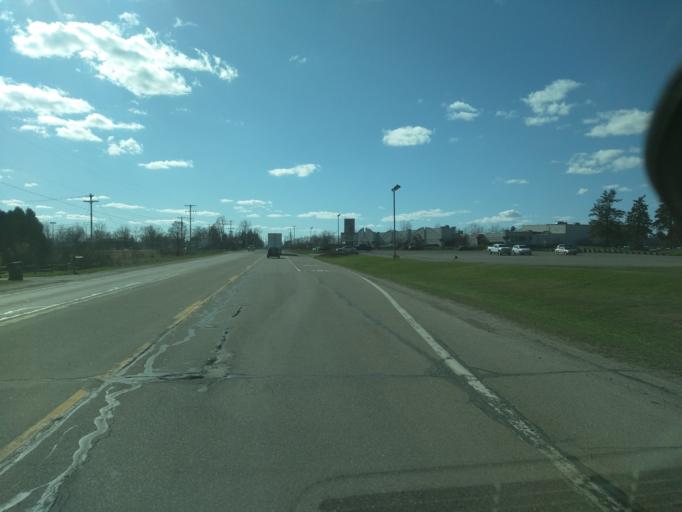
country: US
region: Michigan
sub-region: Ingham County
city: Edgemont Park
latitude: 42.7740
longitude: -84.6136
